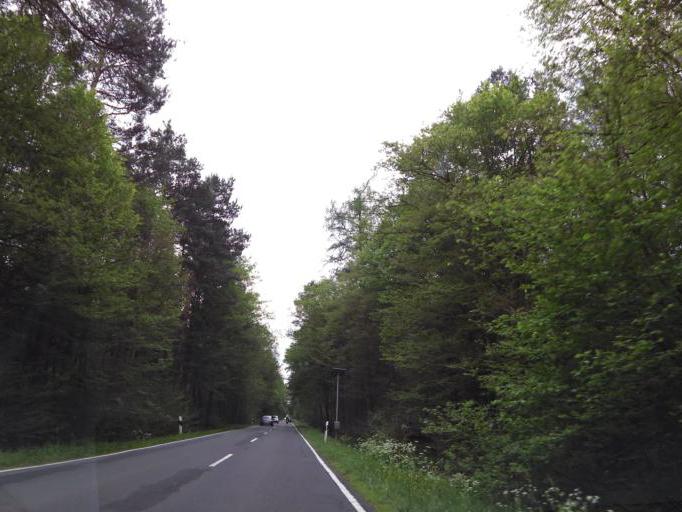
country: DE
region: Hesse
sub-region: Regierungsbezirk Darmstadt
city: Messel
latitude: 49.9583
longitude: 8.7432
